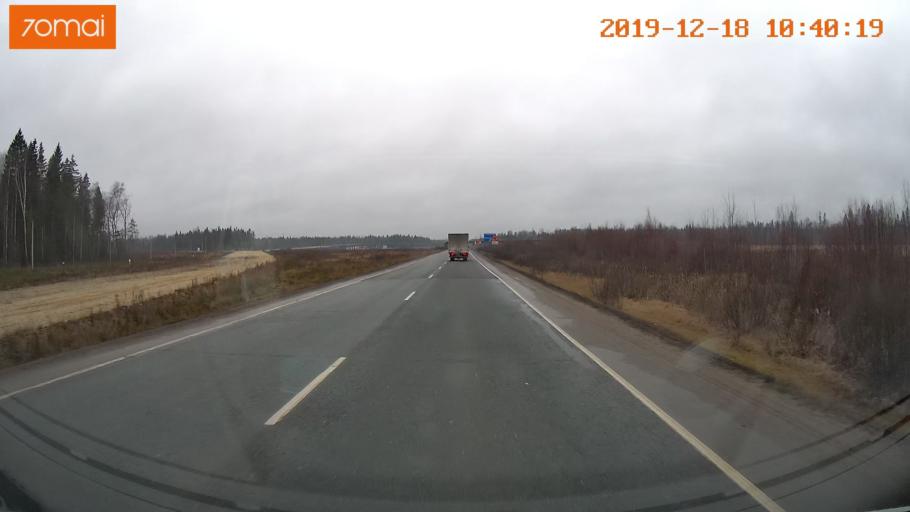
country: RU
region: Moskovskaya
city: Aprelevka
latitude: 55.4500
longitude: 37.1255
